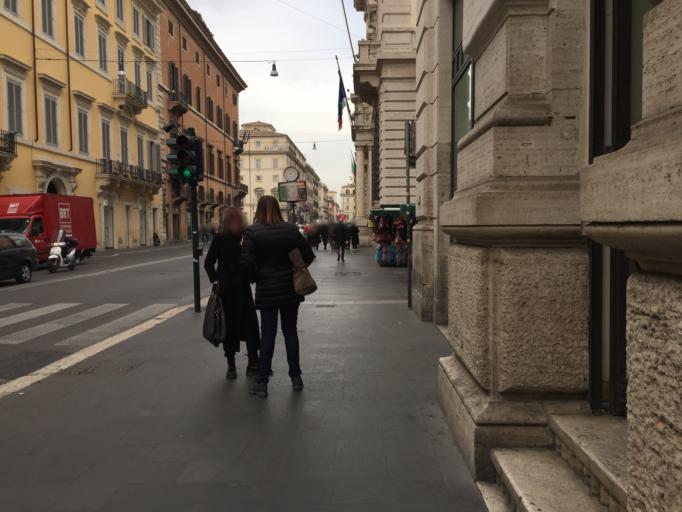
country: VA
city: Vatican City
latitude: 41.9000
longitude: 12.4810
